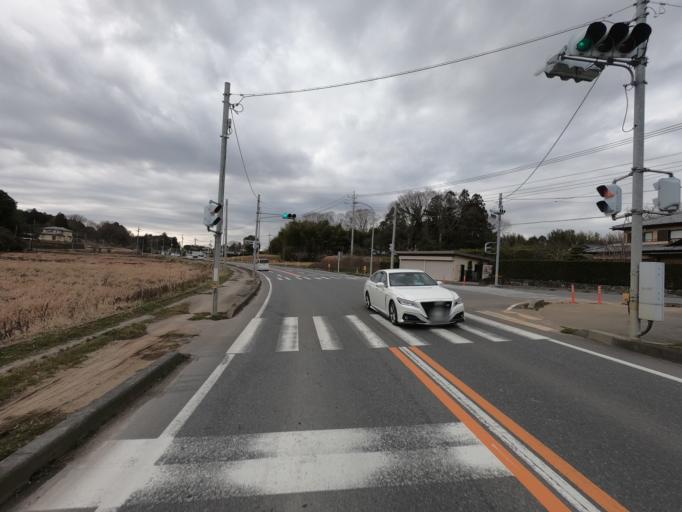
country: JP
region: Ibaraki
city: Ishioka
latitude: 36.0966
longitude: 140.3614
